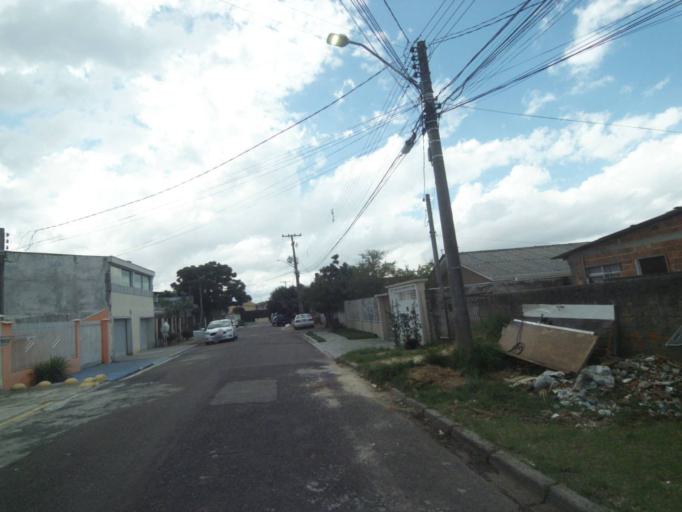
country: BR
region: Parana
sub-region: Pinhais
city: Pinhais
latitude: -25.4466
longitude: -49.2138
